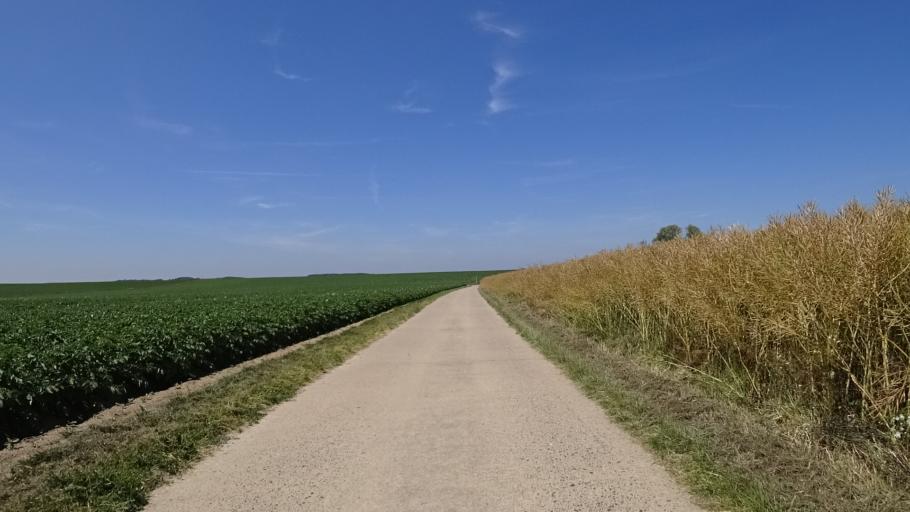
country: BE
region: Wallonia
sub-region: Province du Brabant Wallon
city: Perwez
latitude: 50.6381
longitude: 4.8311
